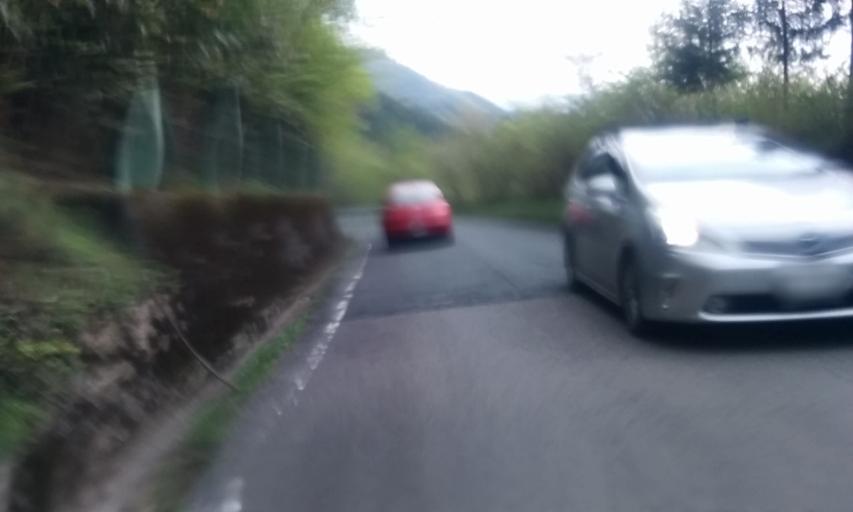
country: JP
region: Ehime
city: Saijo
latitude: 33.8009
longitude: 133.2689
